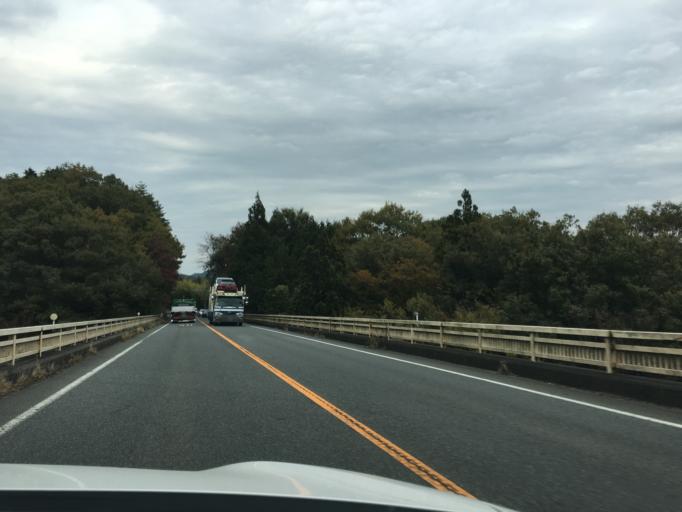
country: JP
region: Fukushima
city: Iwaki
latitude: 37.0773
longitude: 140.7969
